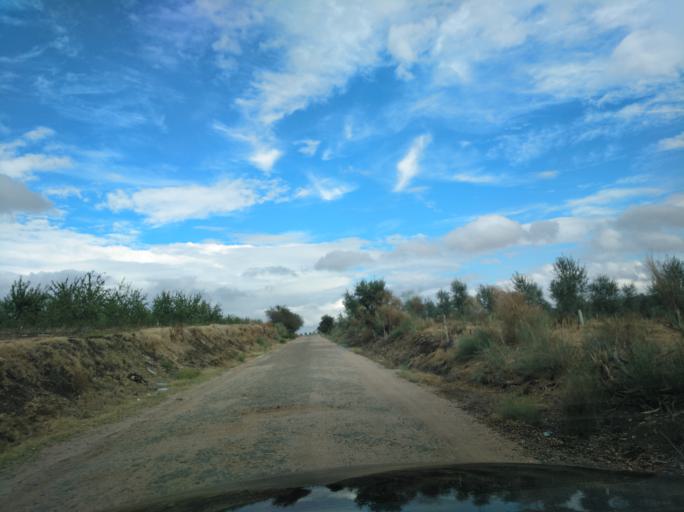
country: PT
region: Portalegre
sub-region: Campo Maior
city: Campo Maior
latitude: 39.0376
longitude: -7.1195
